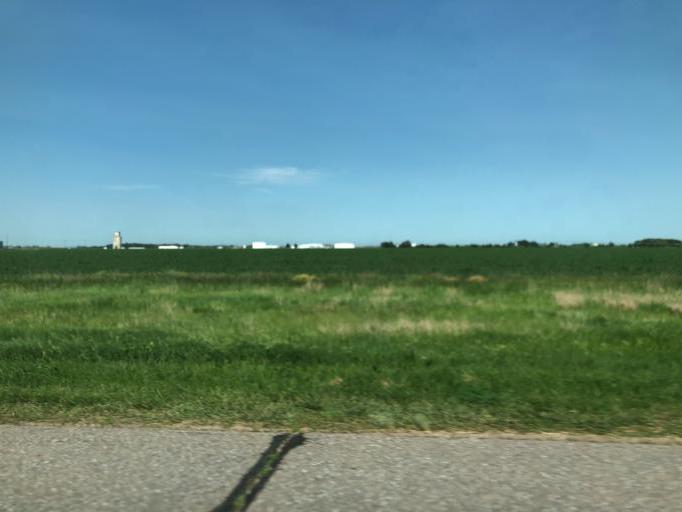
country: US
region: Nebraska
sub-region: York County
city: York
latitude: 40.8106
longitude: -97.5975
